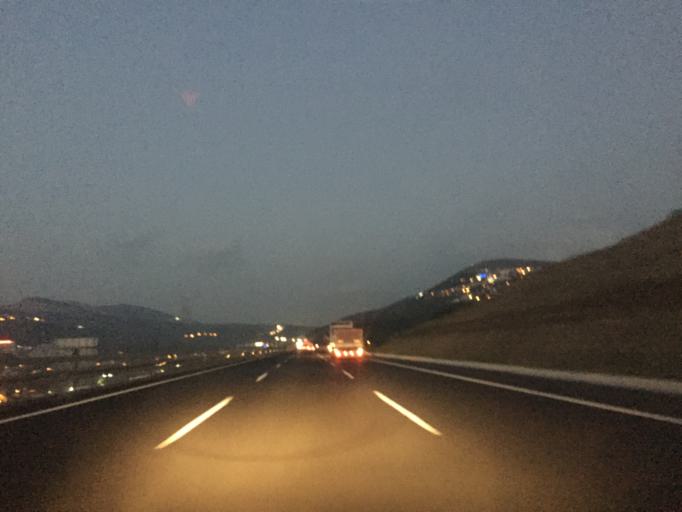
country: TR
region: Bursa
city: Gemlik
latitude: 40.4188
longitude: 29.1593
